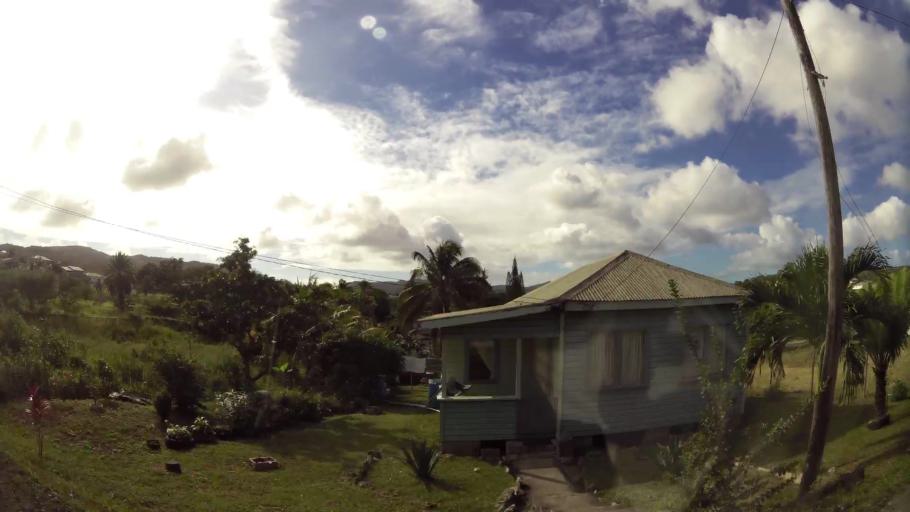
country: AG
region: Saint Peter
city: All Saints
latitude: 17.0504
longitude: -61.7952
